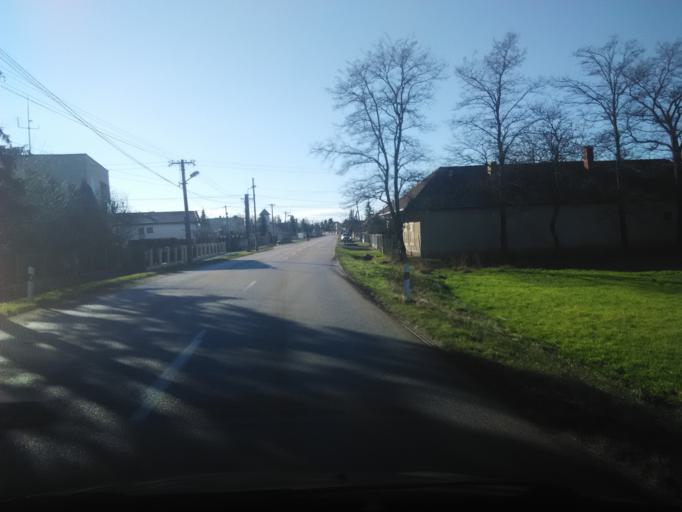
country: SK
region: Nitriansky
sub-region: Okres Nitra
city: Vrable
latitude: 48.2380
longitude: 18.2898
